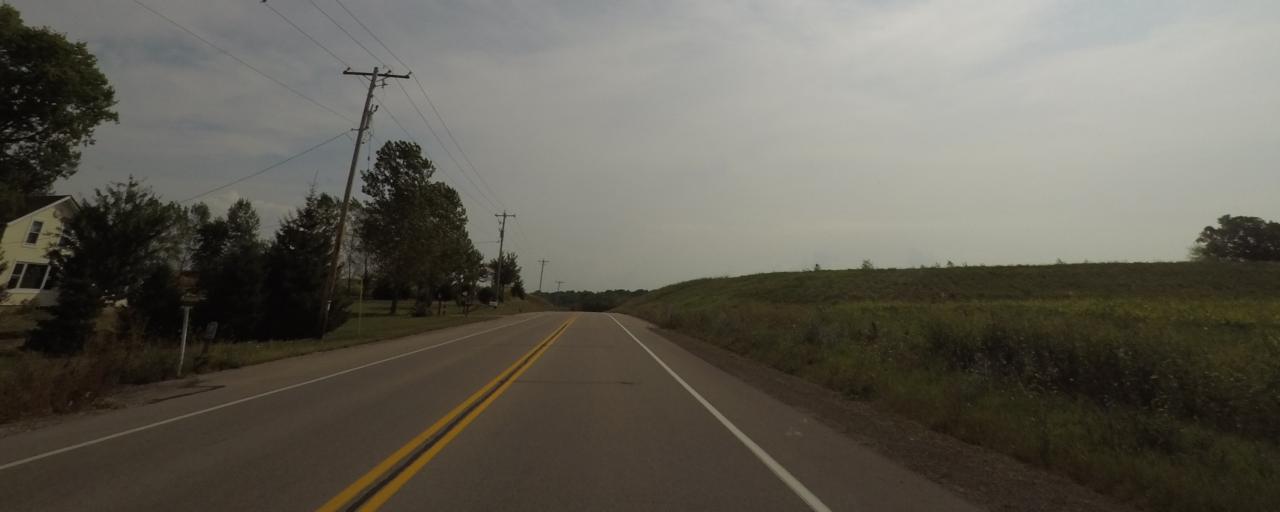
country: US
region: Wisconsin
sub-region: Jefferson County
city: Lake Koshkonong
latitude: 42.9753
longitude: -88.8928
